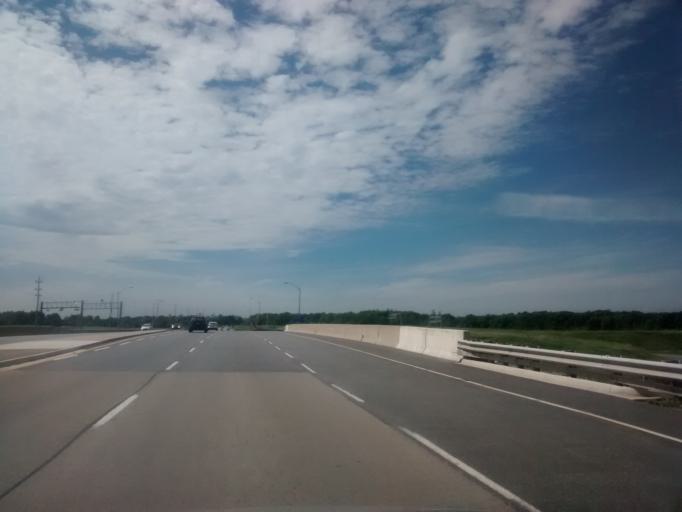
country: CA
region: Ontario
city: Burlington
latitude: 43.4150
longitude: -79.8196
